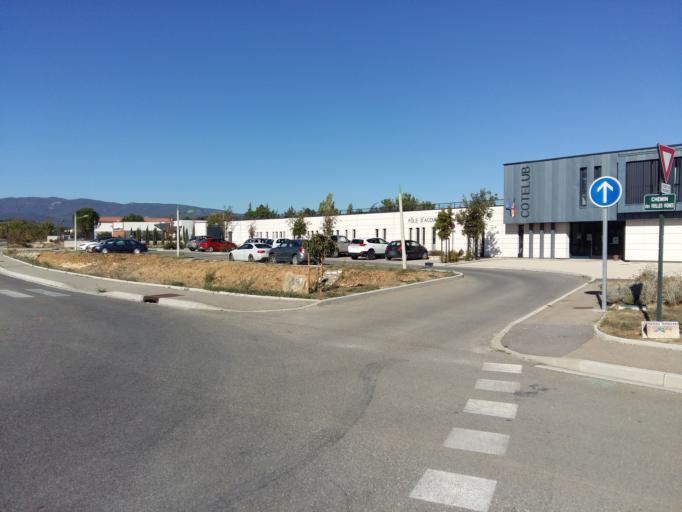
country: FR
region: Provence-Alpes-Cote d'Azur
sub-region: Departement du Vaucluse
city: Pertuis
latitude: 43.7228
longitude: 5.5398
